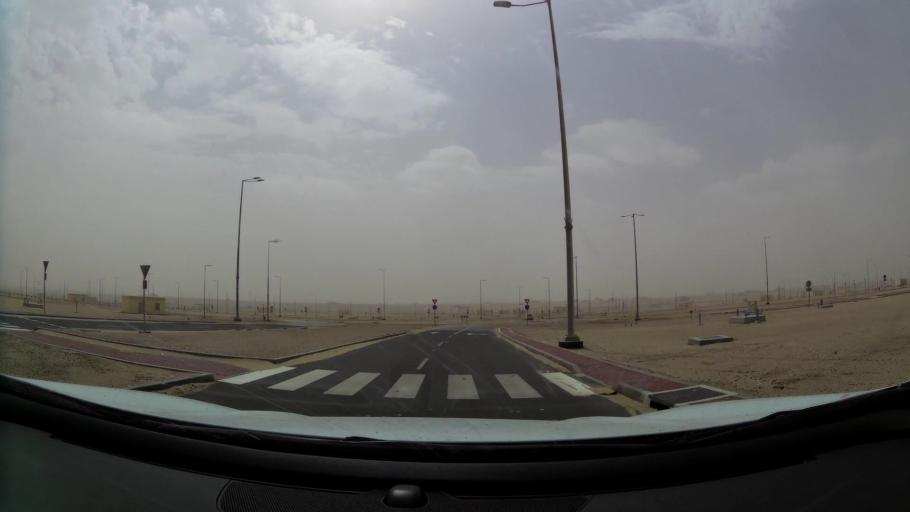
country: AE
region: Abu Dhabi
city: Abu Dhabi
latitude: 24.3487
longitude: 54.7622
